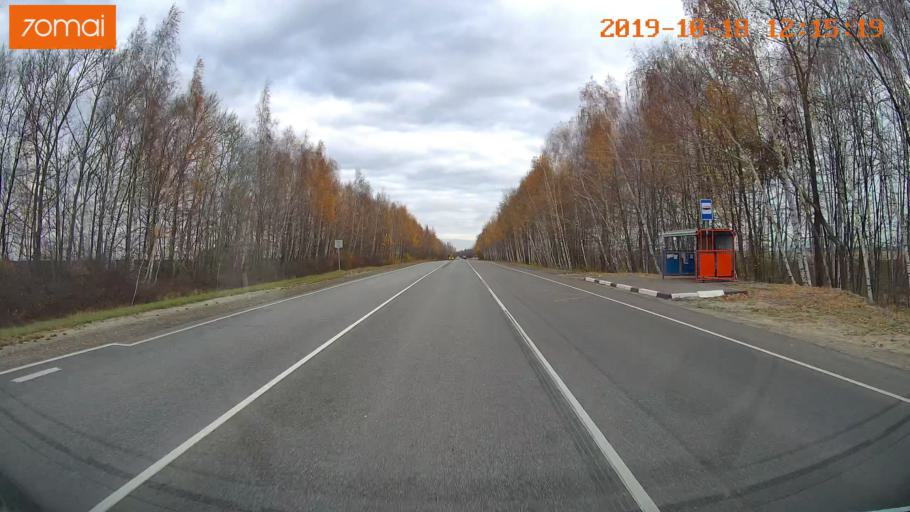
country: RU
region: Rjazan
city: Zakharovo
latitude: 54.4417
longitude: 39.3980
